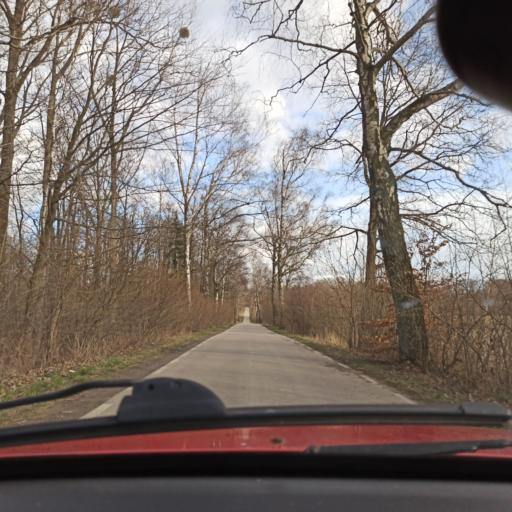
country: PL
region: Warmian-Masurian Voivodeship
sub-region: Powiat elblaski
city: Tolkmicko
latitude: 54.2620
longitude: 19.4944
